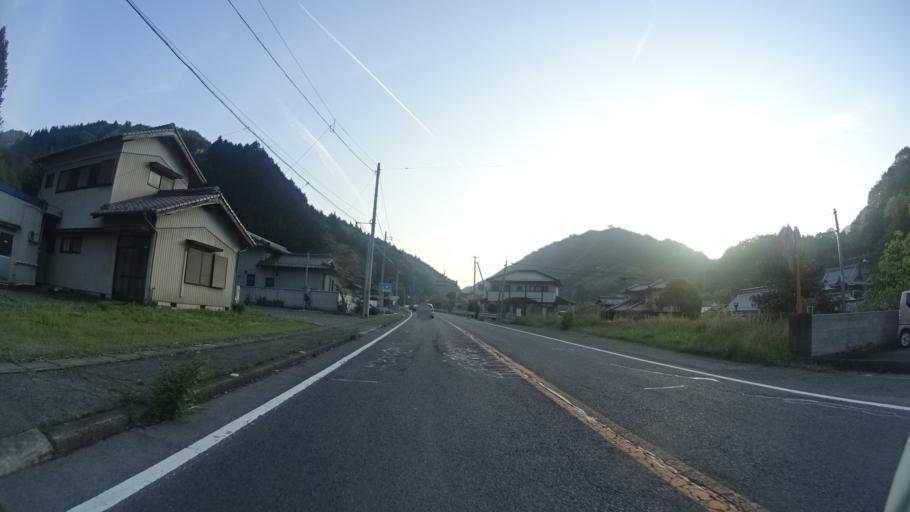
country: JP
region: Tokushima
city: Ikedacho
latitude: 34.0027
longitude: 133.7076
